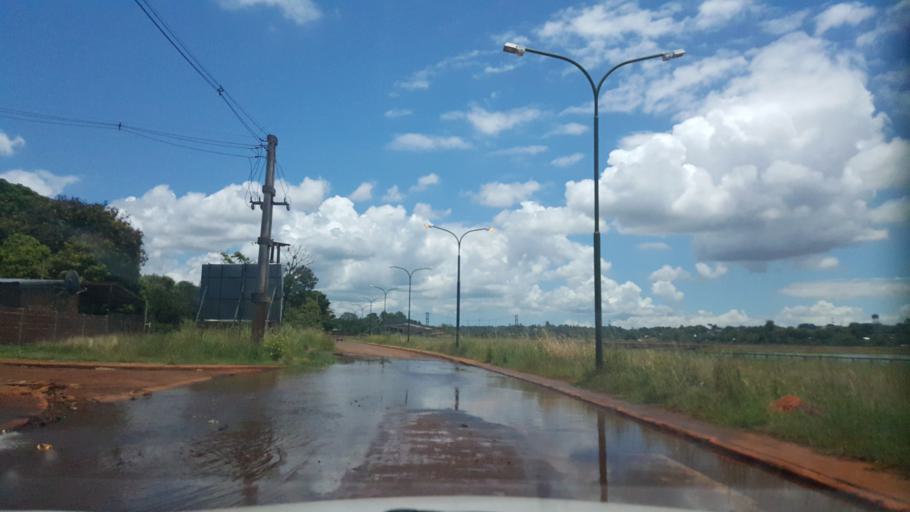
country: AR
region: Misiones
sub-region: Departamento de Capital
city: Posadas
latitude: -27.4211
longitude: -55.8960
